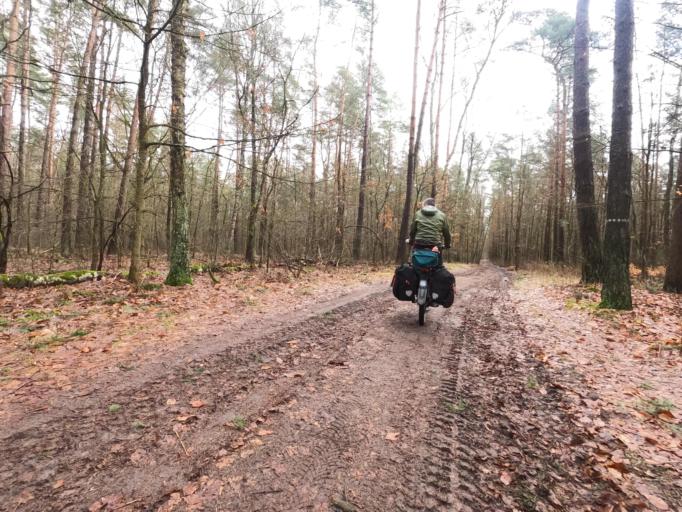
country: PL
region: Greater Poland Voivodeship
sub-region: Powiat pilski
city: Smilowo
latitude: 53.1133
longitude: 16.9272
